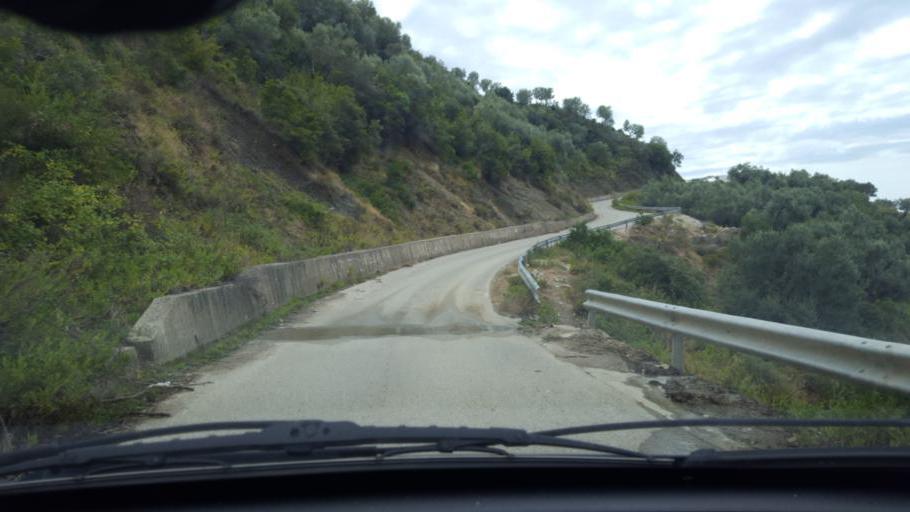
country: AL
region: Vlore
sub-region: Rrethi i Sarandes
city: Lukove
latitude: 39.9844
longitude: 19.9168
